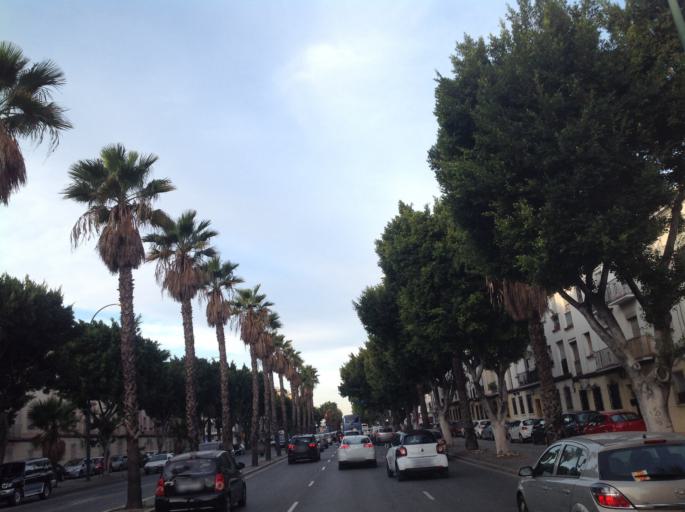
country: ES
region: Andalusia
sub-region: Provincia de Malaga
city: Malaga
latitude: 36.7159
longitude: -4.4441
